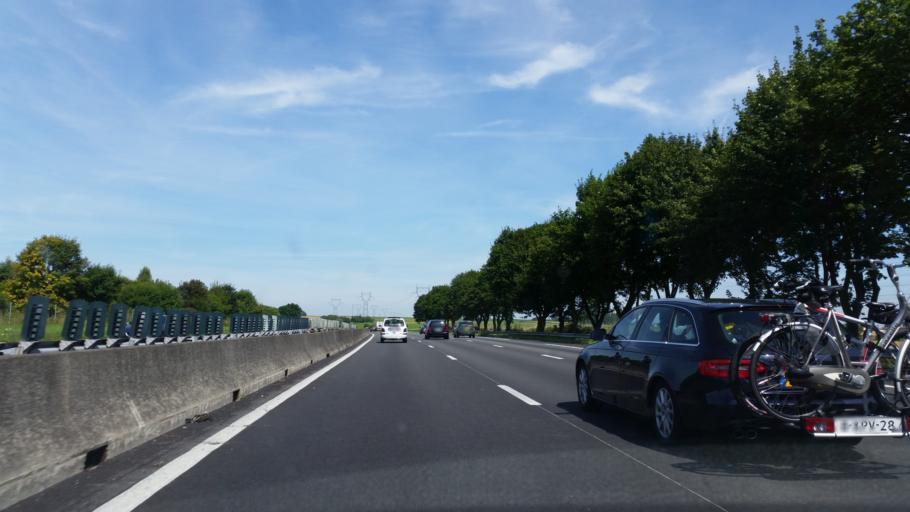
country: FR
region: Picardie
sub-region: Departement de la Somme
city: Peronne
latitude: 49.9023
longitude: 2.8485
